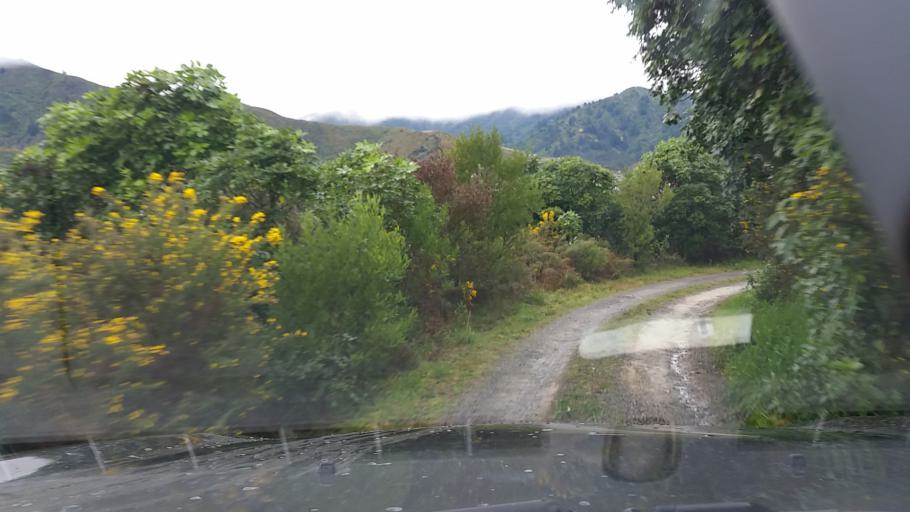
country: NZ
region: Marlborough
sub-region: Marlborough District
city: Picton
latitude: -41.2645
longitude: 174.0373
